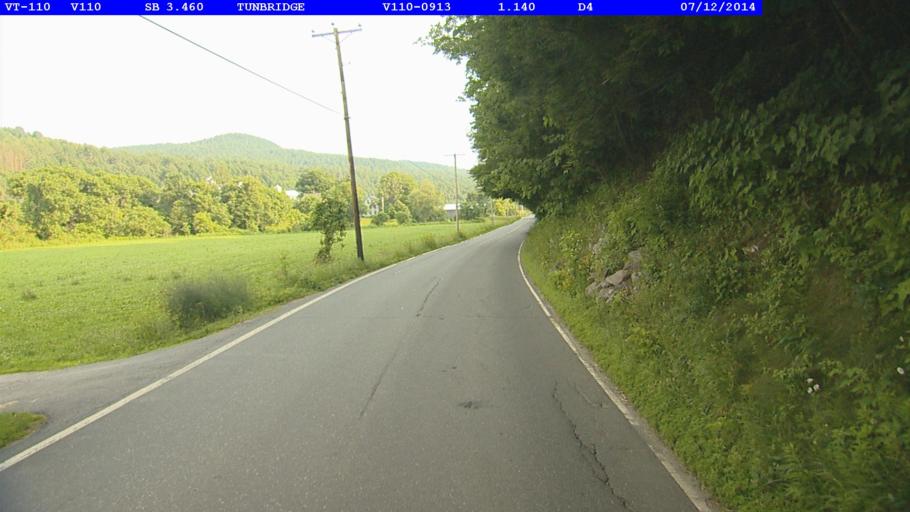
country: US
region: Vermont
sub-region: Orange County
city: Chelsea
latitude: 43.8672
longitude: -72.4990
